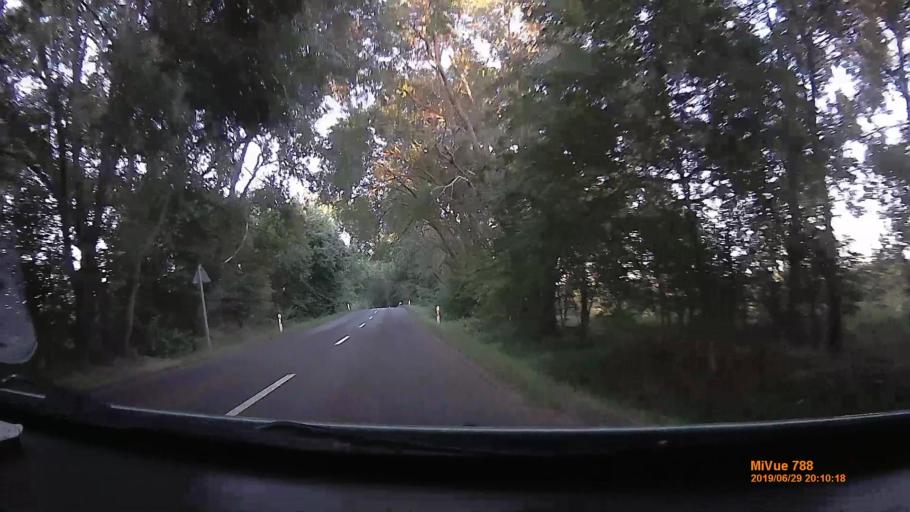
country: HU
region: Pest
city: Perbal
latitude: 47.5363
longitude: 18.7738
